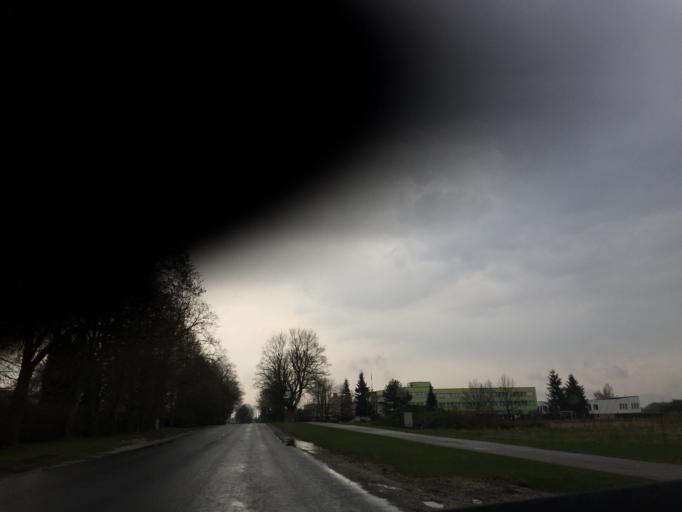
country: EE
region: Tartu
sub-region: UElenurme vald
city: Ulenurme
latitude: 58.3194
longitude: 26.7212
